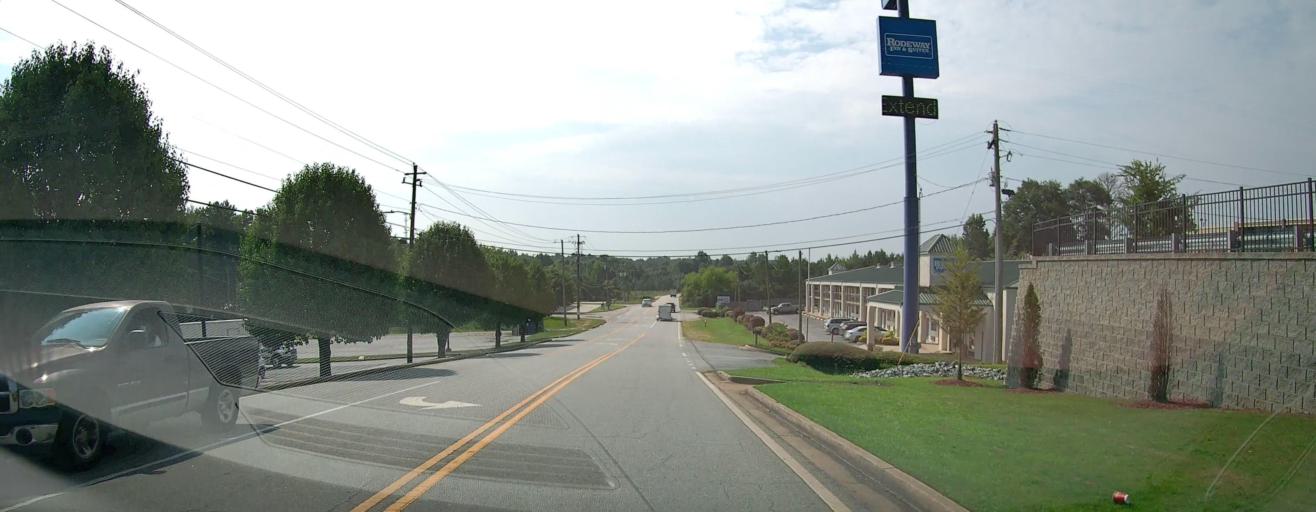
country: US
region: Georgia
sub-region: Bibb County
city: West Point
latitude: 32.8104
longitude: -83.7225
